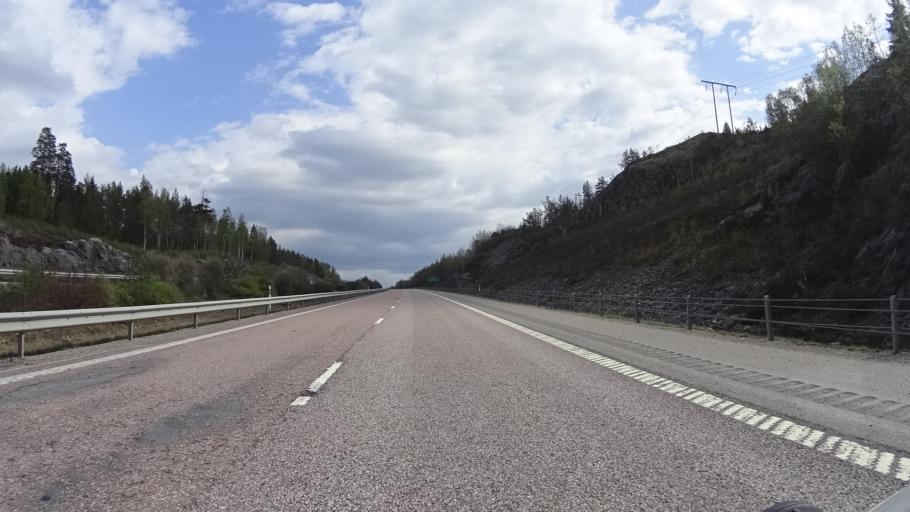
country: SE
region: Soedermanland
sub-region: Strangnas Kommun
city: Mariefred
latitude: 59.2371
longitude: 17.1849
